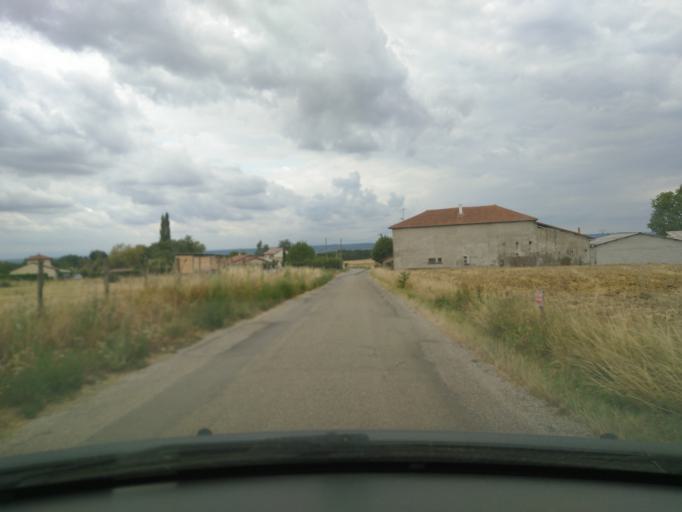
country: FR
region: Rhone-Alpes
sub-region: Departement de l'Isere
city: Beaurepaire
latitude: 45.3817
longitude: 4.9936
